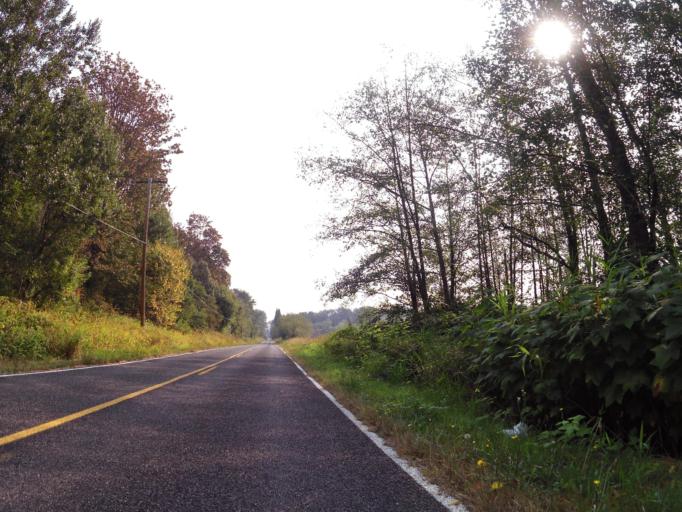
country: US
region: Washington
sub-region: Whatcom County
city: Birch Bay
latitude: 48.8631
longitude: -122.7227
